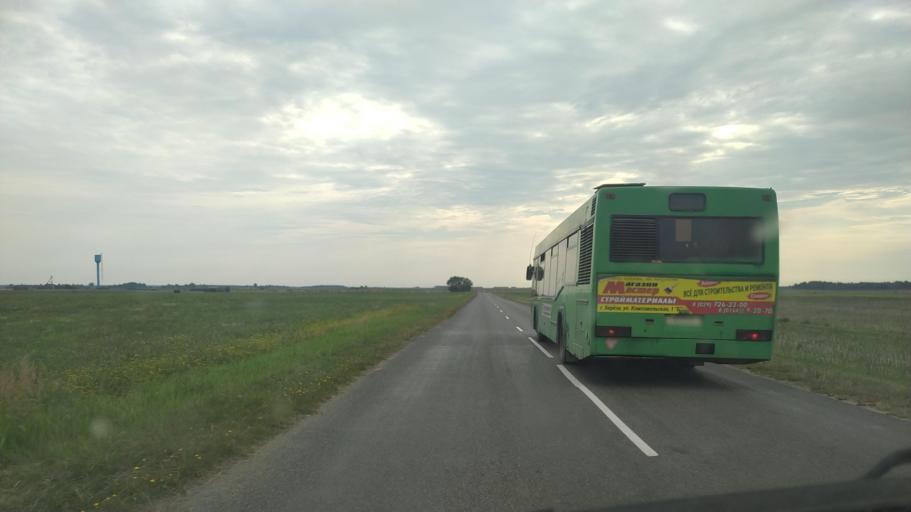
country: BY
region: Brest
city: Byaroza
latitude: 52.5767
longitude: 24.8626
